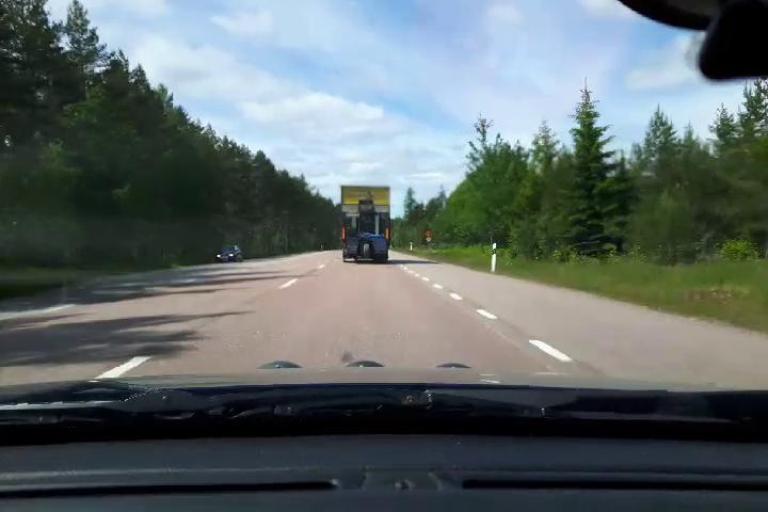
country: SE
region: Uppsala
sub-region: Osthammars Kommun
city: Bjorklinge
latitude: 60.1110
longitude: 17.5312
